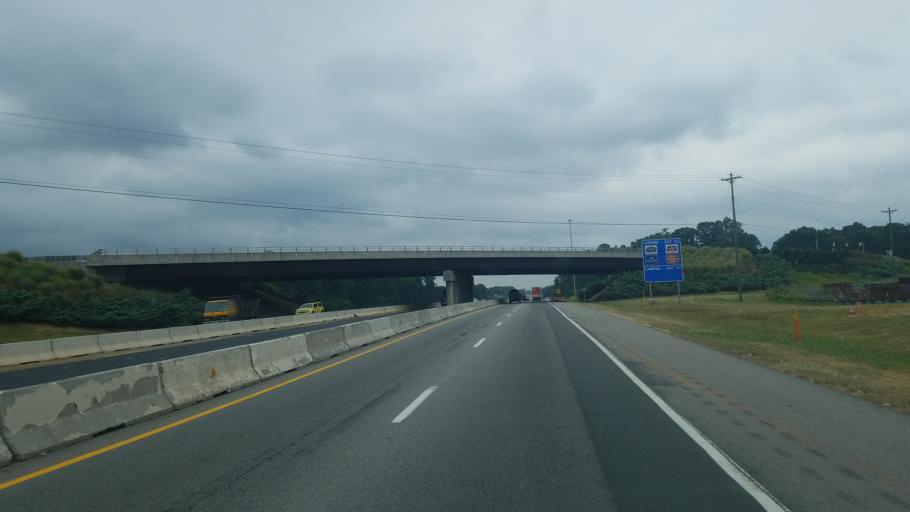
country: US
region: North Carolina
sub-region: Gaston County
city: Davidson
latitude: 35.5294
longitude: -80.8625
